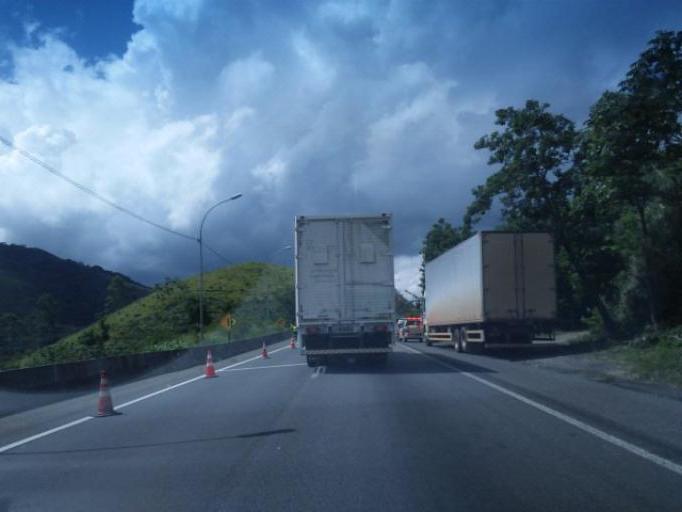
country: BR
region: Sao Paulo
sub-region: Cajati
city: Cajati
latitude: -24.8339
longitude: -48.2145
